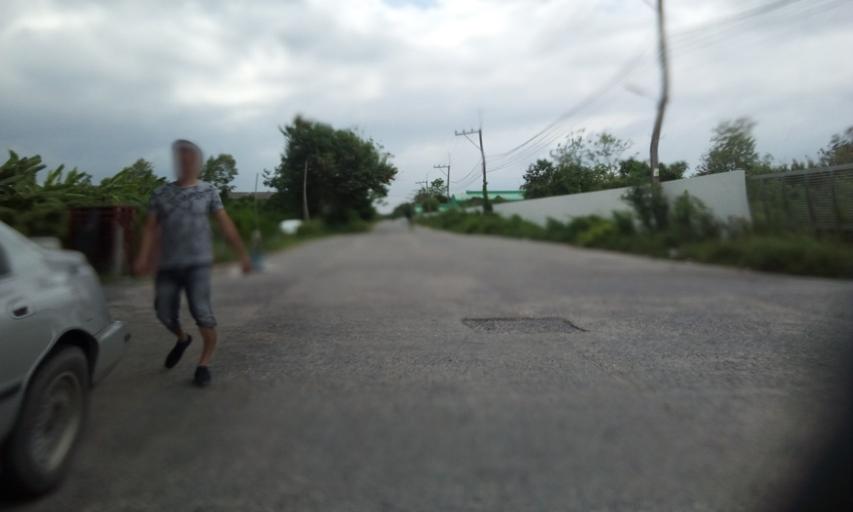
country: TH
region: Pathum Thani
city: Nong Suea
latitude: 14.0586
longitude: 100.8354
